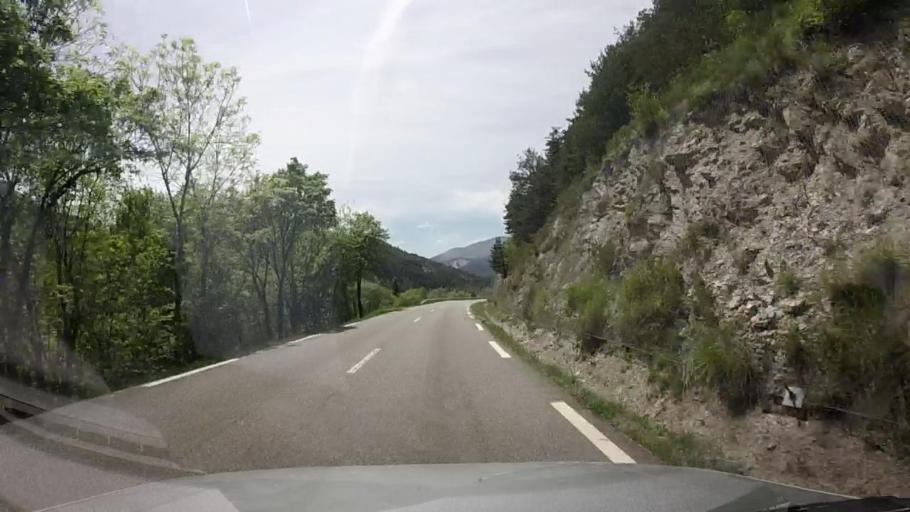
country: FR
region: Provence-Alpes-Cote d'Azur
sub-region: Departement des Alpes-de-Haute-Provence
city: Seyne-les-Alpes
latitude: 44.2737
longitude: 6.3853
